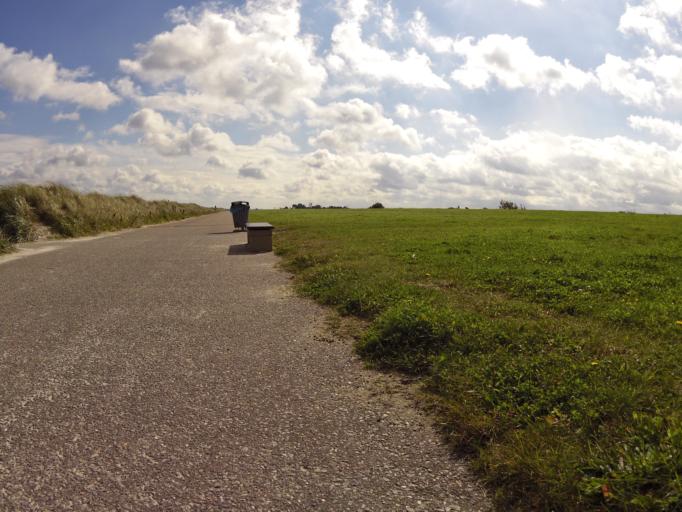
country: DE
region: Schleswig-Holstein
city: Wisch
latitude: 54.4248
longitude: 10.3913
